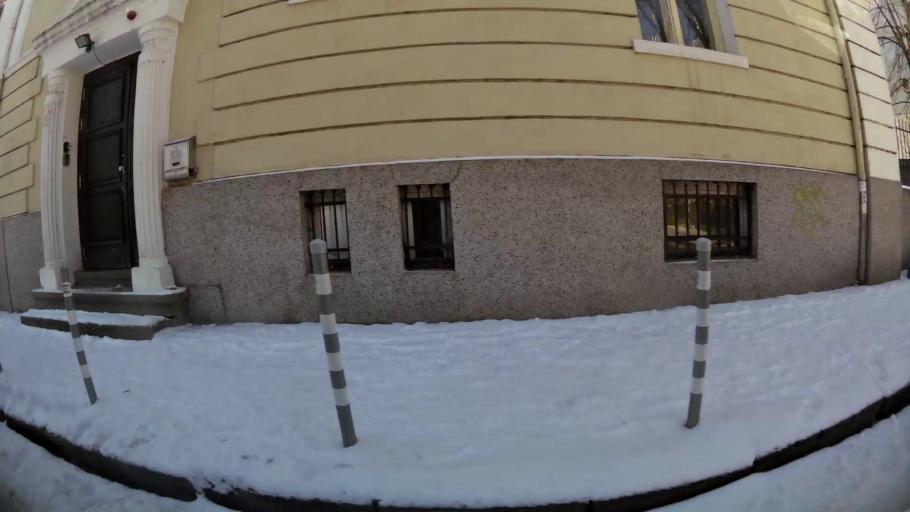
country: BG
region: Sofia-Capital
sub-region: Stolichna Obshtina
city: Sofia
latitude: 42.6833
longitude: 23.3255
